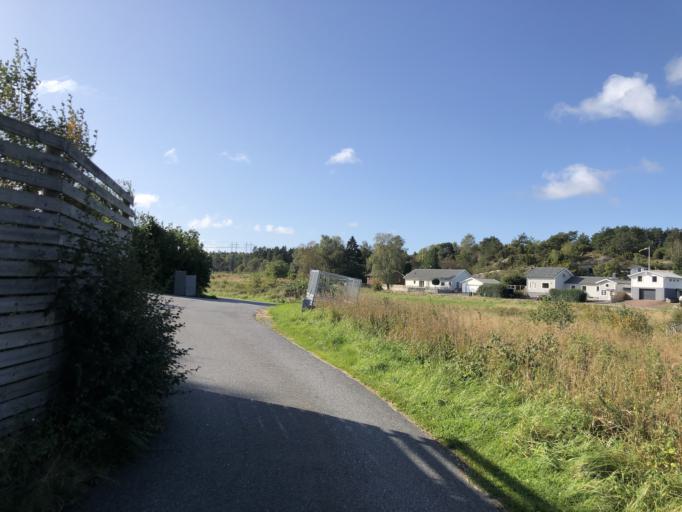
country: SE
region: Vaestra Goetaland
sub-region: Goteborg
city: Torslanda
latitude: 57.7346
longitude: 11.8156
